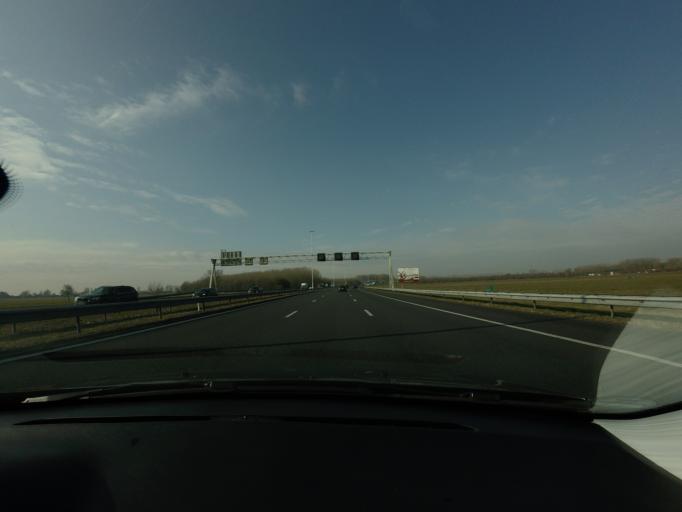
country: NL
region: Utrecht
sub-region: Gemeente Vianen
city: Vianen
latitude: 51.9562
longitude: 5.0719
